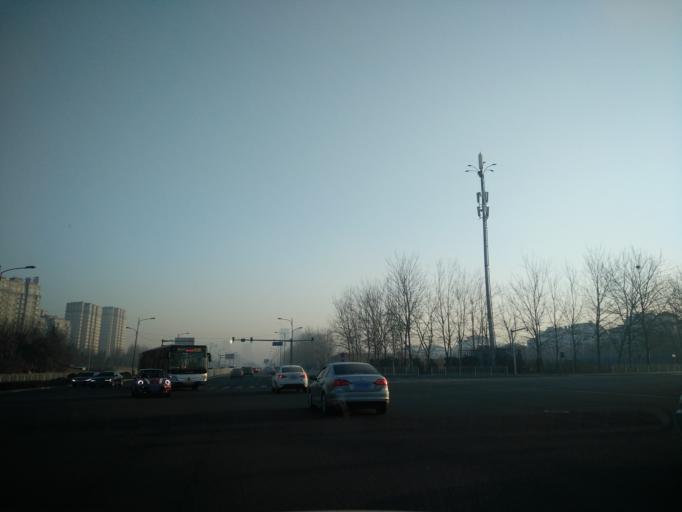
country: CN
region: Beijing
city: Jiugong
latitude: 39.7789
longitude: 116.4777
